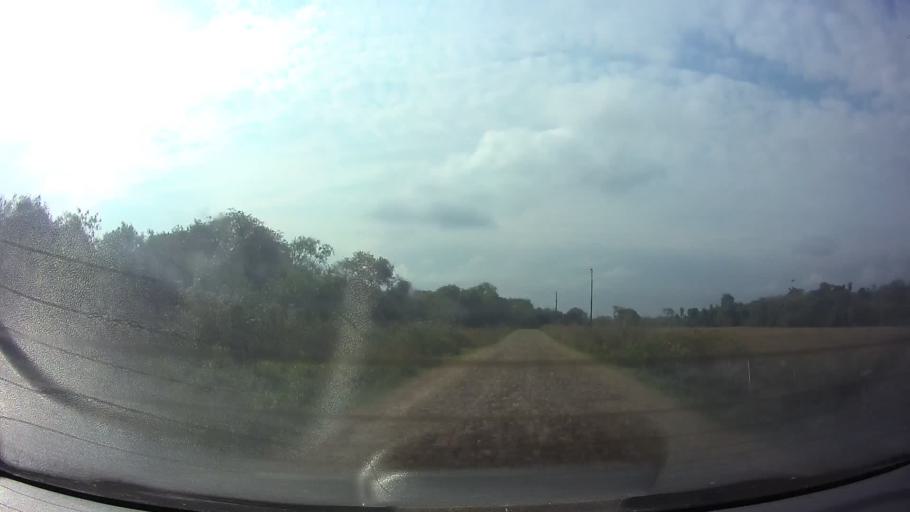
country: PY
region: Cordillera
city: Arroyos y Esteros
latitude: -25.0053
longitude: -57.1996
